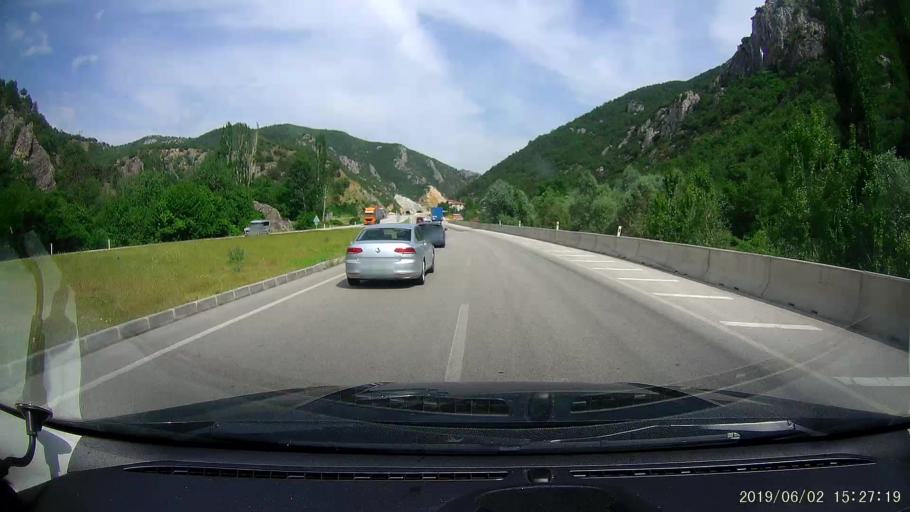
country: TR
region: Amasya
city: Saraycik
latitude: 40.9836
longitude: 35.0553
